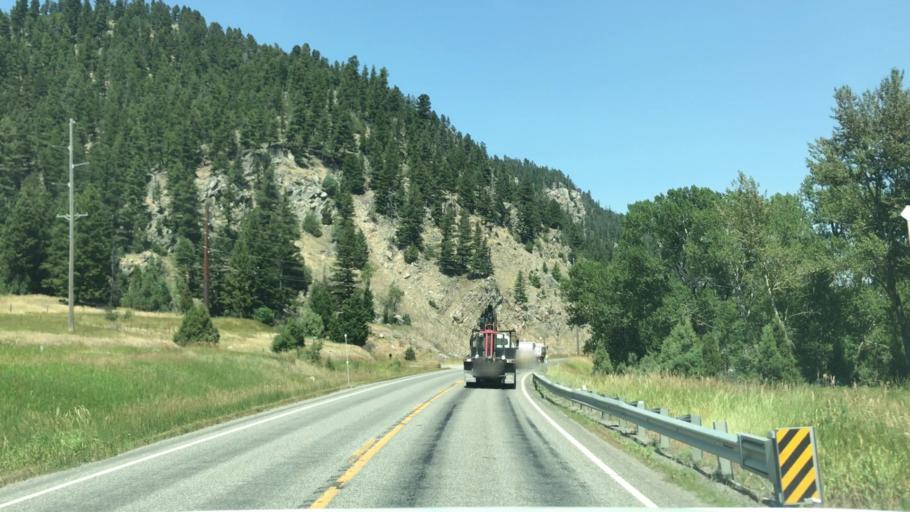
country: US
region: Montana
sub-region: Gallatin County
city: Four Corners
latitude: 45.4994
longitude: -111.2709
